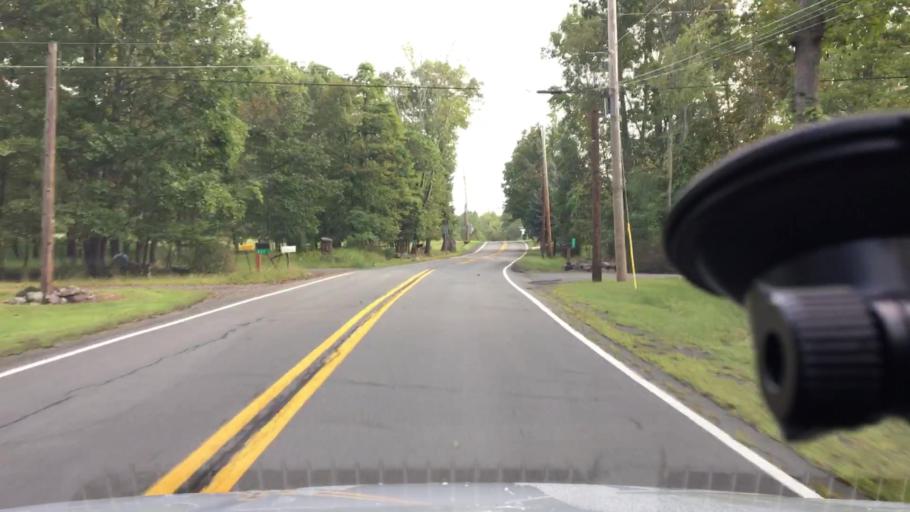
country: US
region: Pennsylvania
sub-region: Monroe County
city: Mountainhome
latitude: 41.1434
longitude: -75.2580
